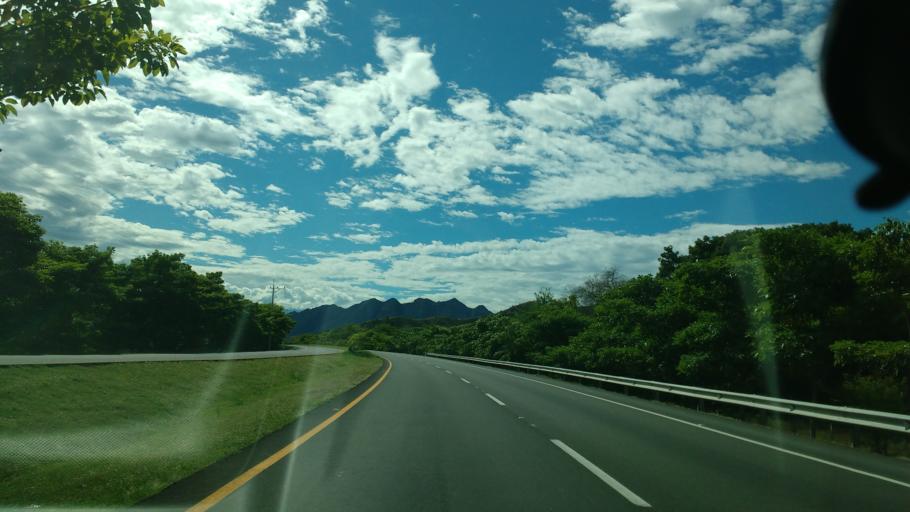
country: CO
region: Tolima
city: Espinal
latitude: 4.2484
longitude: -74.9836
